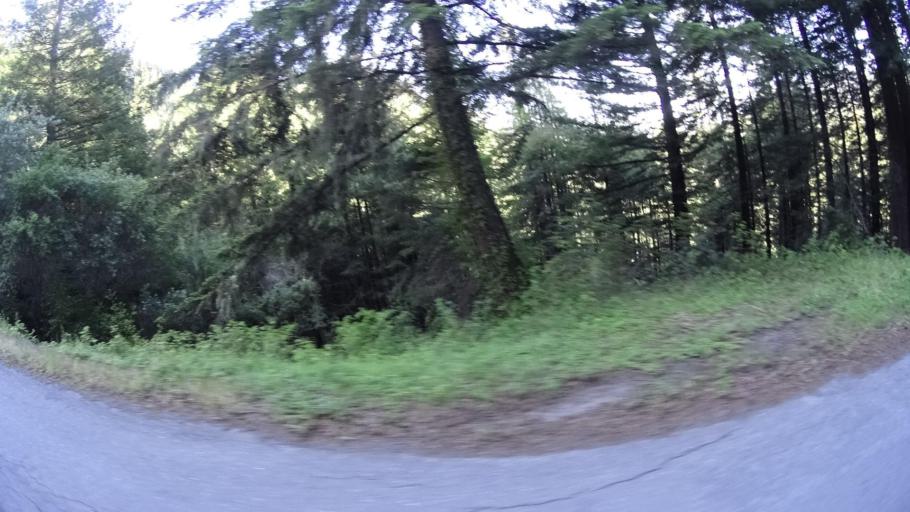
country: US
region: California
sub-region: Humboldt County
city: Rio Dell
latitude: 40.4512
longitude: -123.9802
